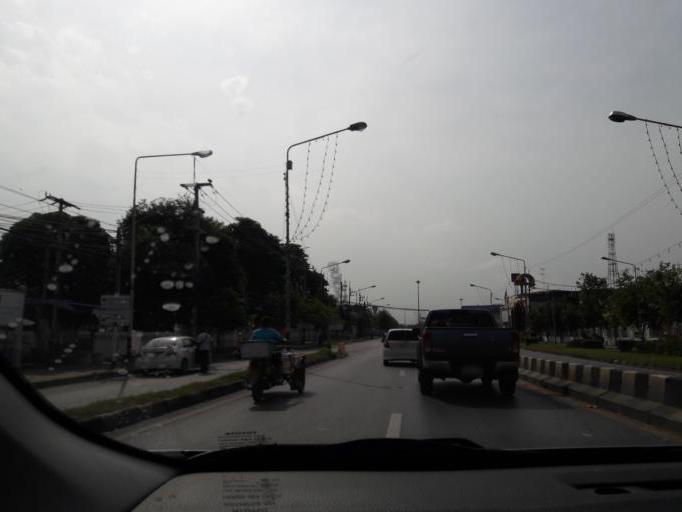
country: TH
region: Ang Thong
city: Ang Thong
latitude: 14.5888
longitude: 100.4541
